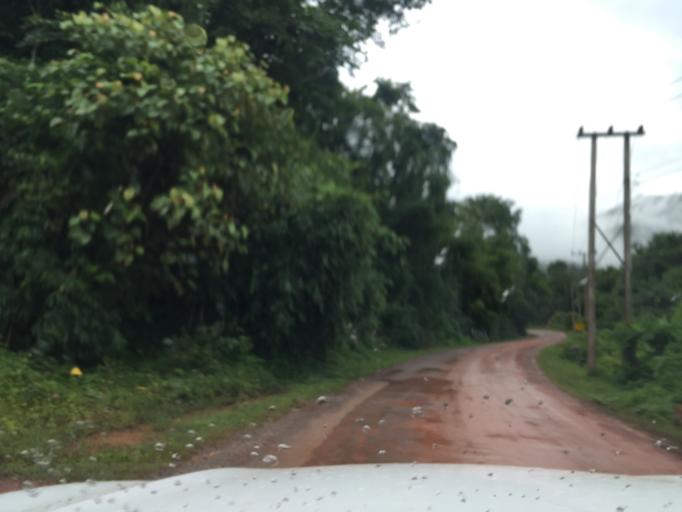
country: LA
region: Oudomxai
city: Muang La
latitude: 20.8405
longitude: 102.1039
